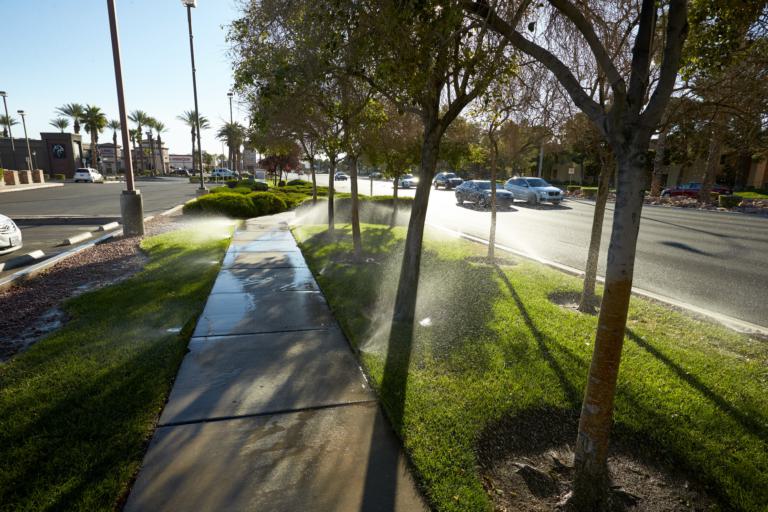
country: US
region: Nevada
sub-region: Clark County
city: Summerlin South
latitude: 36.1446
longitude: -115.3011
